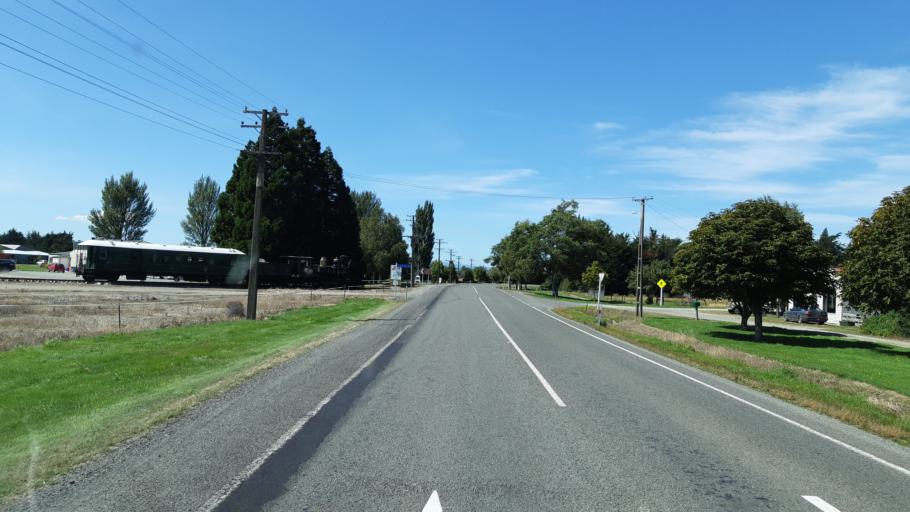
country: NZ
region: Southland
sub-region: Gore District
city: Gore
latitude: -45.9927
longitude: 168.8087
